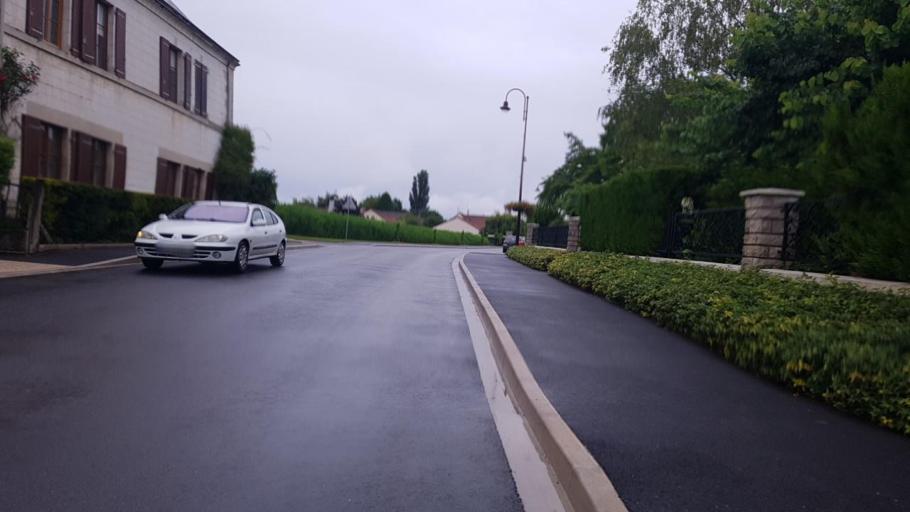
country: FR
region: Champagne-Ardenne
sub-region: Departement de la Marne
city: Sarry
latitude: 48.9213
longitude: 4.4014
